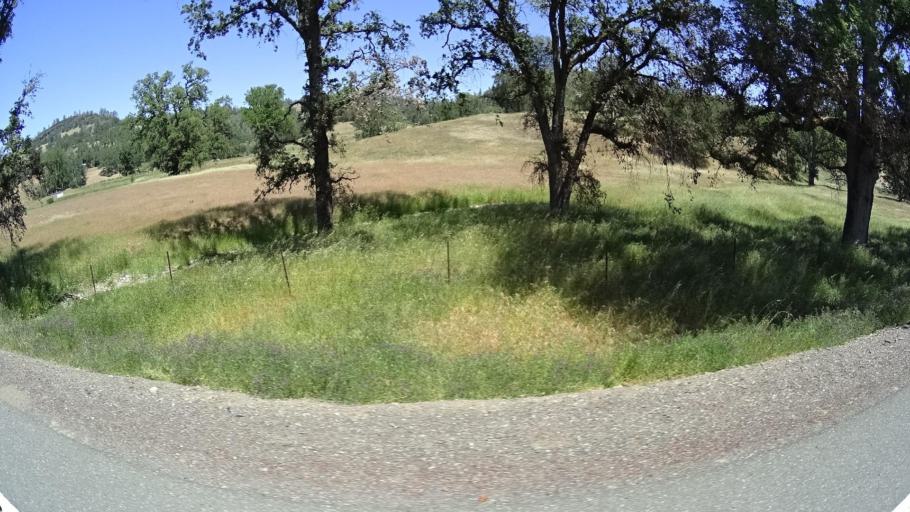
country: US
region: California
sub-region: Lake County
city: Hidden Valley Lake
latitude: 38.8458
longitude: -122.6088
